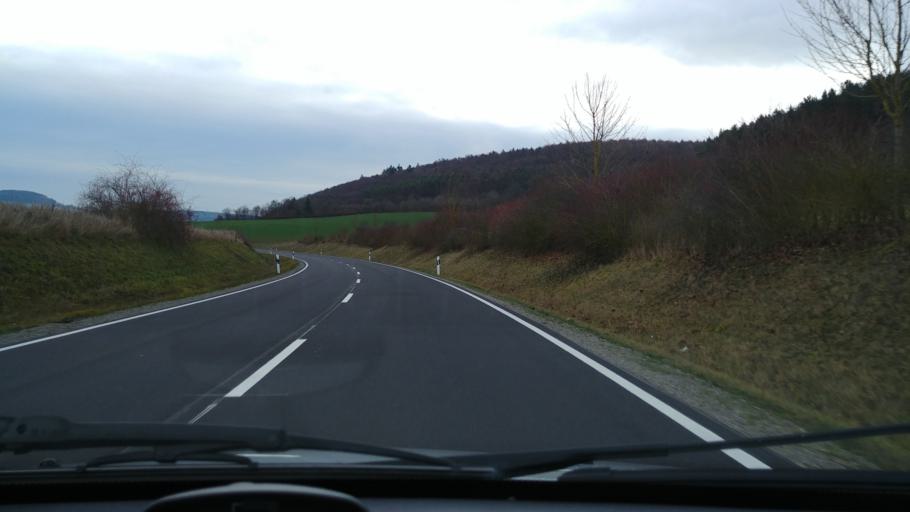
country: DE
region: Bavaria
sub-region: Regierungsbezirk Unterfranken
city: Karlstadt
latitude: 49.9747
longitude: 9.7431
